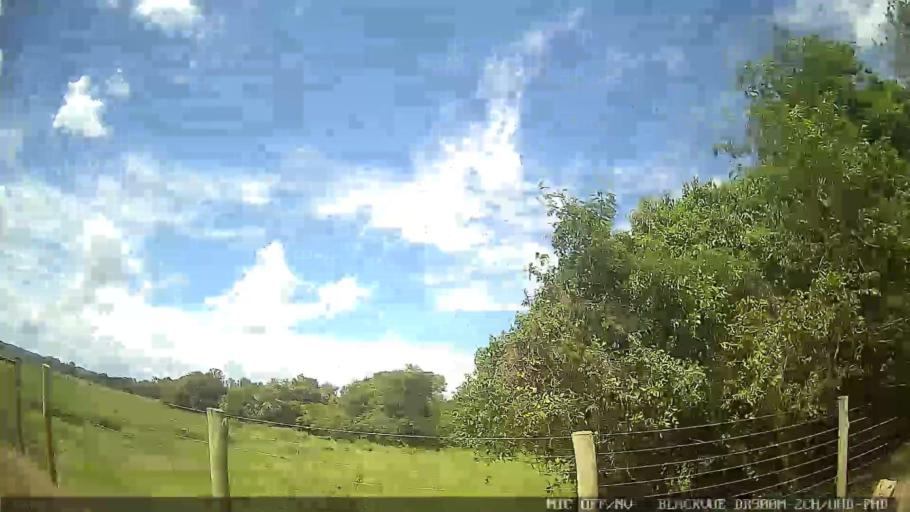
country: BR
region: Sao Paulo
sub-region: Conchas
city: Conchas
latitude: -23.0559
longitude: -47.9819
